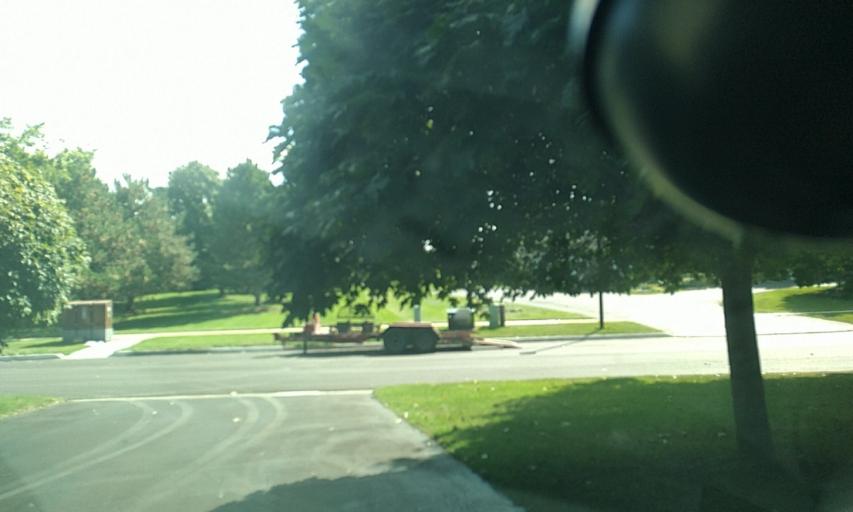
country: CA
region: Ontario
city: Newmarket
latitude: 44.1001
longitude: -79.4319
